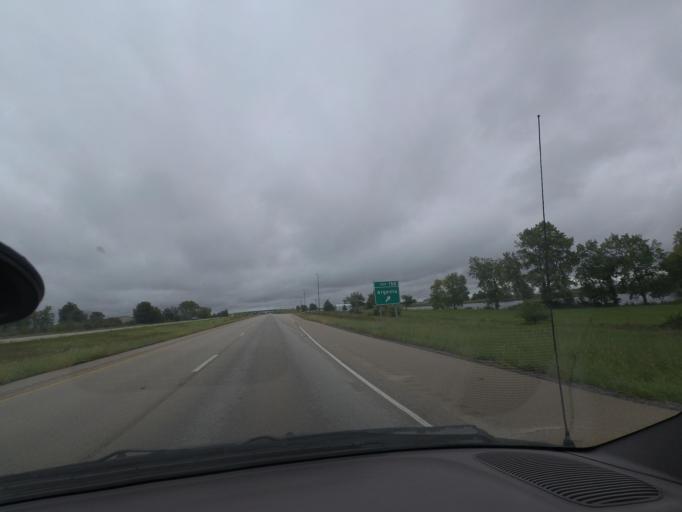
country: US
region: Illinois
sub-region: Piatt County
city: Cerro Gordo
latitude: 39.9500
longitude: -88.8268
